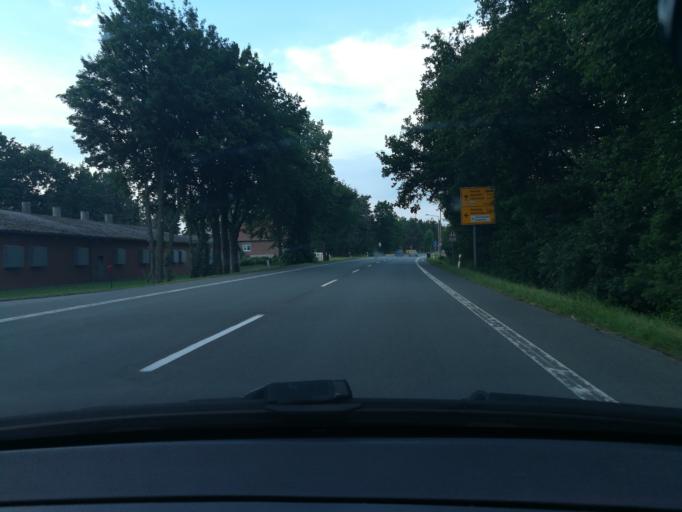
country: DE
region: North Rhine-Westphalia
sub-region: Regierungsbezirk Detmold
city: Hovelhof
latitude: 51.8765
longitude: 8.6748
